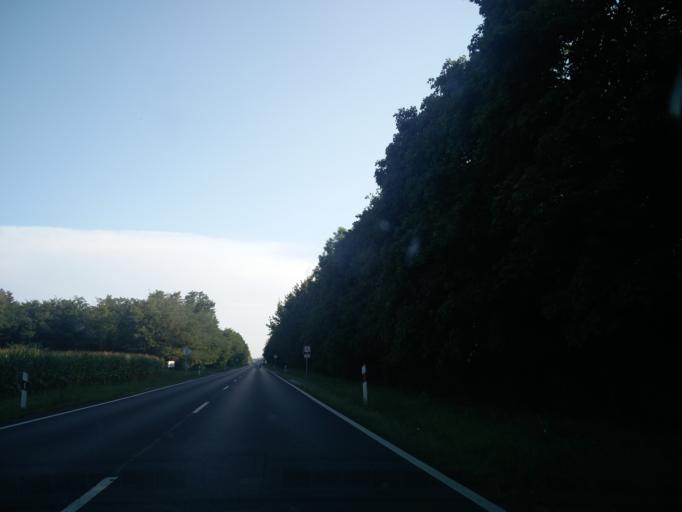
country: HU
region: Zala
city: Zalaegerszeg
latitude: 46.8723
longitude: 16.8534
